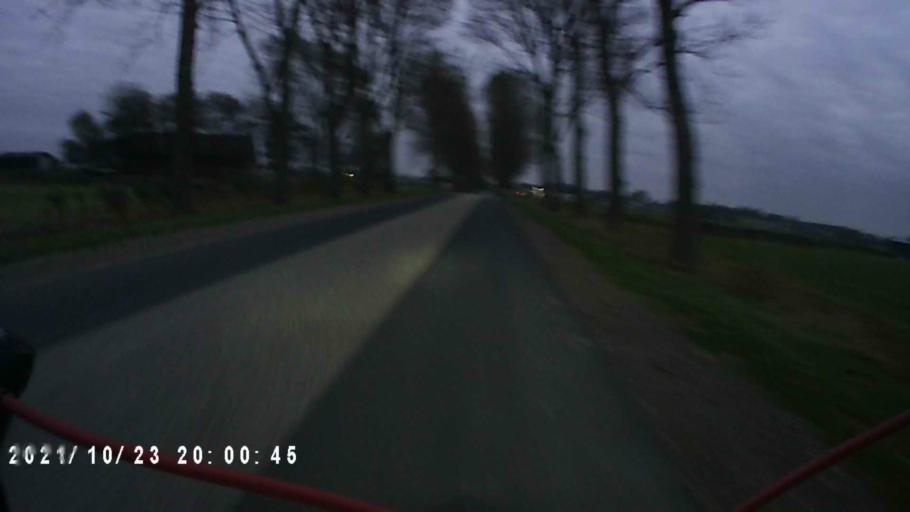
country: NL
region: Friesland
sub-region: Gemeente Harlingen
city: Harlingen
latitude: 53.1077
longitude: 5.4618
